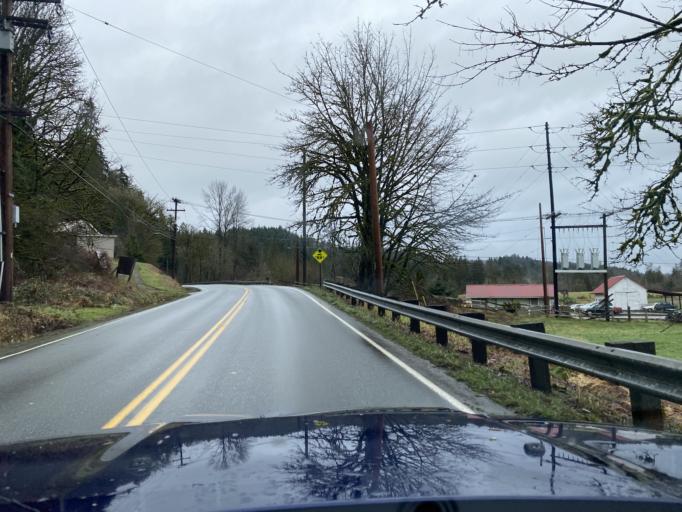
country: US
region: Washington
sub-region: King County
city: Duvall
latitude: 47.7320
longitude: -122.0119
